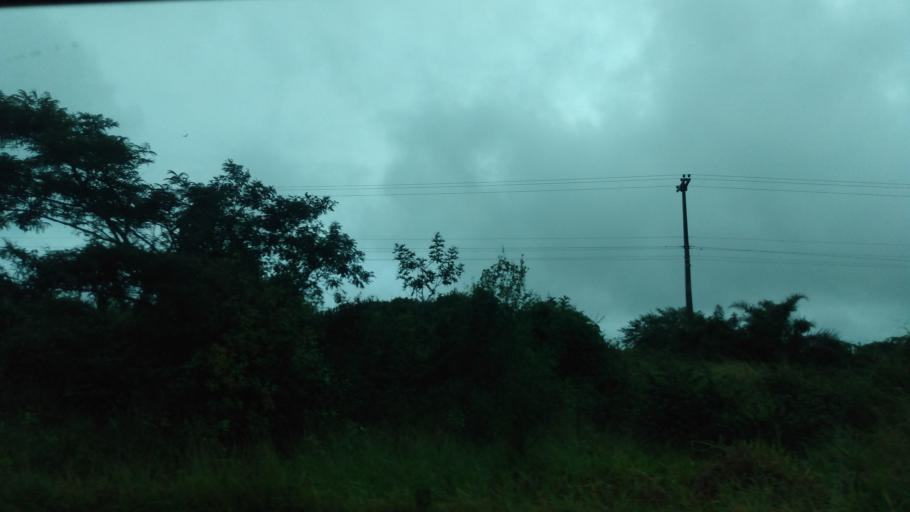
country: BR
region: Pernambuco
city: Garanhuns
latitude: -8.8746
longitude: -36.5266
